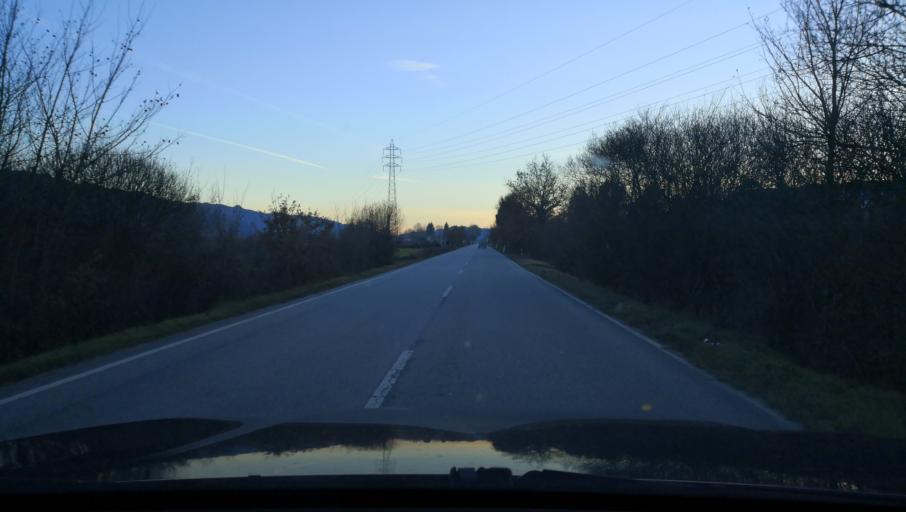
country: PT
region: Vila Real
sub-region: Vila Pouca de Aguiar
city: Vila Pouca de Aguiar
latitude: 41.4565
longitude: -7.6666
